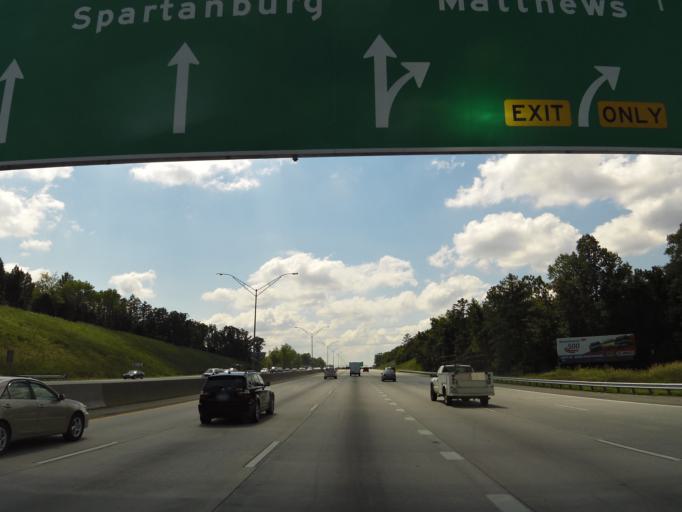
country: US
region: North Carolina
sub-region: Cabarrus County
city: Harrisburg
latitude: 35.3617
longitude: -80.7207
